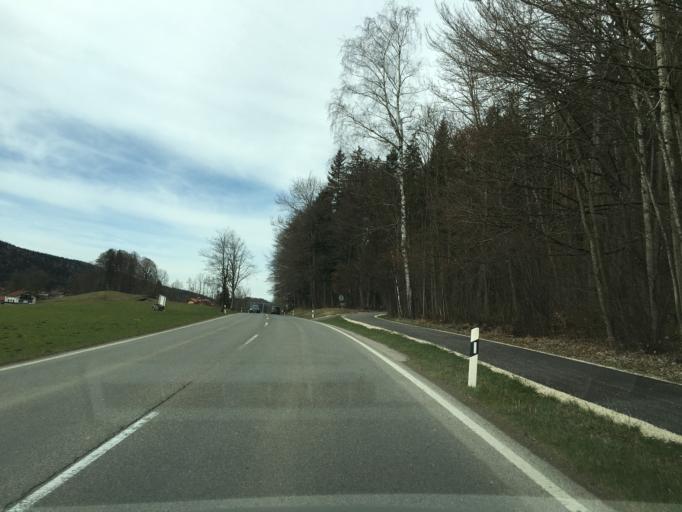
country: DE
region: Bavaria
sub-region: Upper Bavaria
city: Inzell
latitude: 47.7798
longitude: 12.7393
